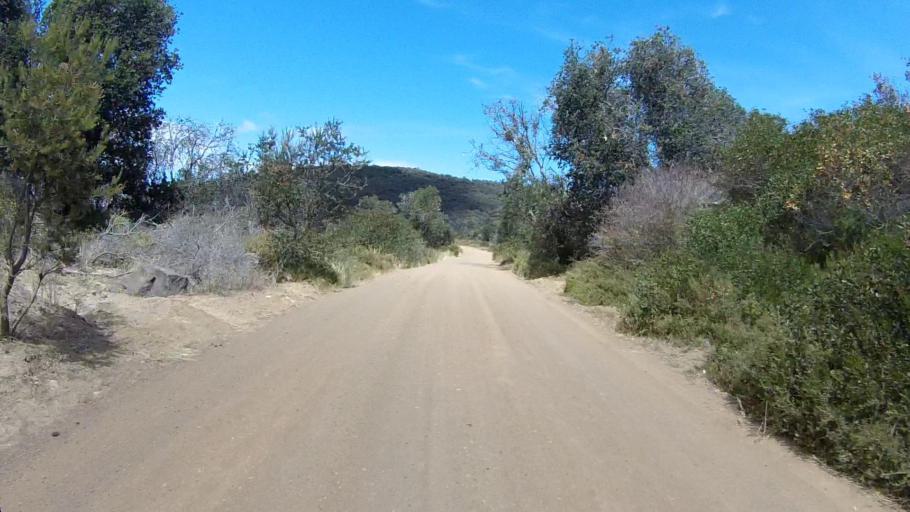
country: AU
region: Tasmania
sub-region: Sorell
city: Sorell
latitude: -42.8742
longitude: 147.6450
